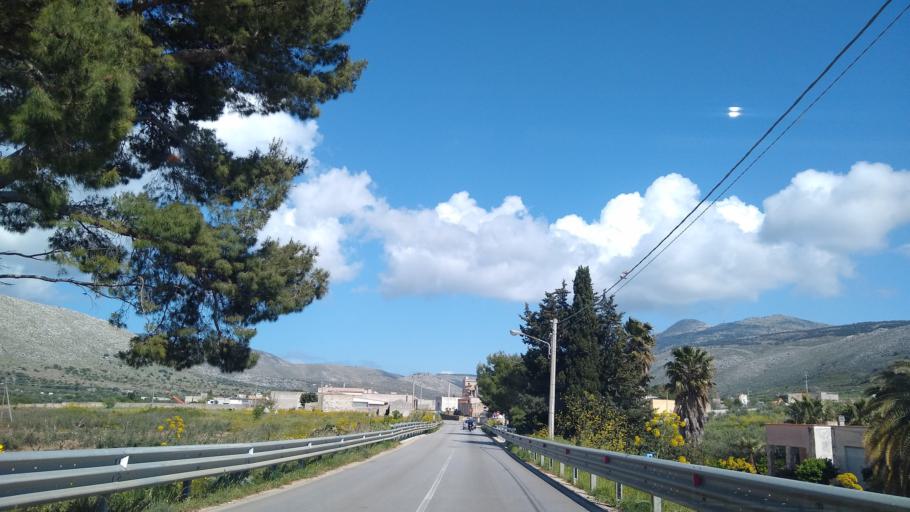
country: IT
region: Sicily
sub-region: Trapani
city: Custonaci
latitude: 38.0800
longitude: 12.7096
